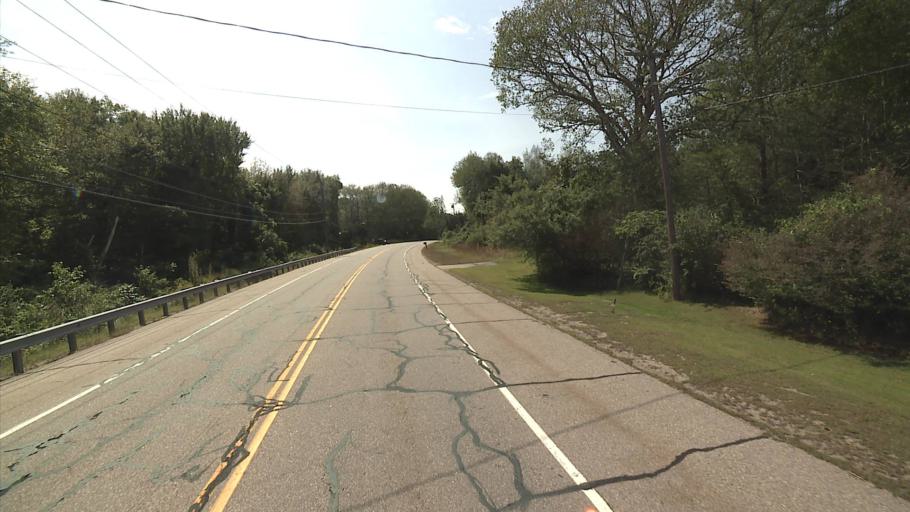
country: US
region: Connecticut
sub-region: New London County
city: Lisbon
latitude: 41.5939
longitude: -72.0193
